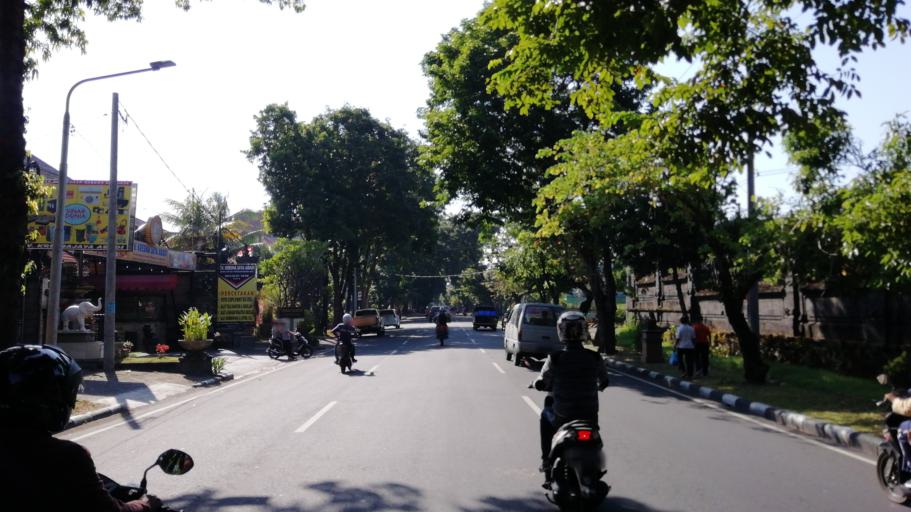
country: ID
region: Bali
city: Dajan Tangluk
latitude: -8.6673
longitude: 115.2352
